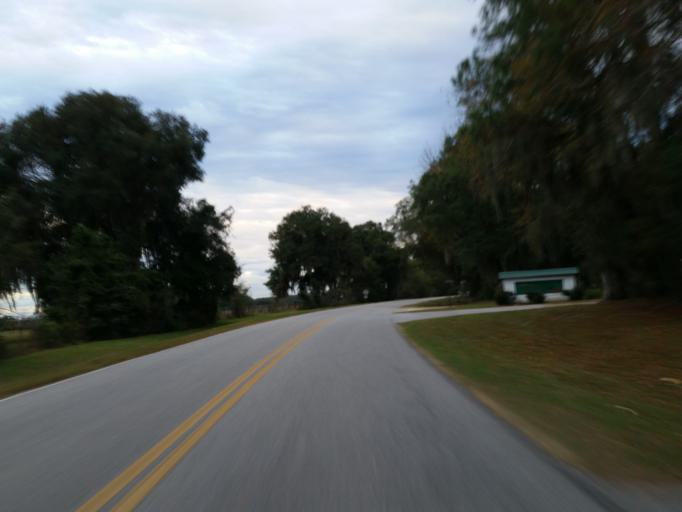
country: US
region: Florida
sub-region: Hamilton County
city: Jasper
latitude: 30.5448
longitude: -83.1029
